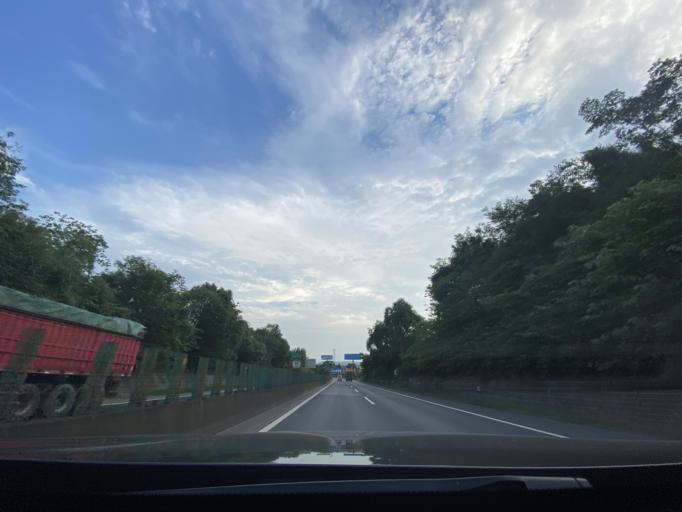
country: CN
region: Sichuan
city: Luojiang
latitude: 31.3917
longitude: 104.5580
